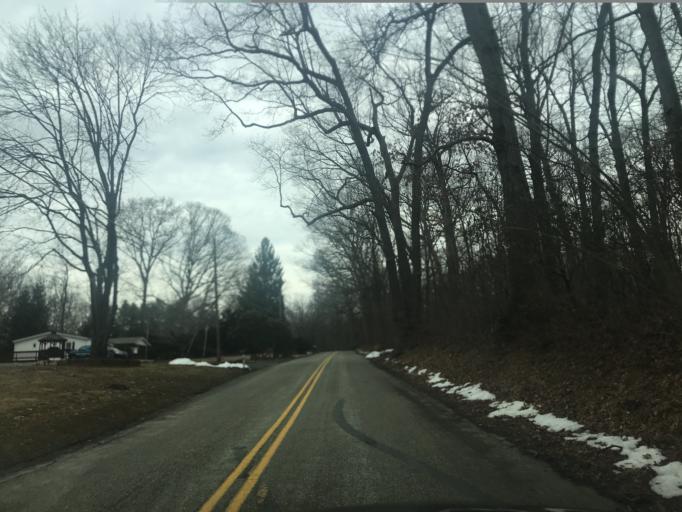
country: US
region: Maryland
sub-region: Harford County
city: Jarrettsville
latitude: 39.6528
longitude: -76.4059
